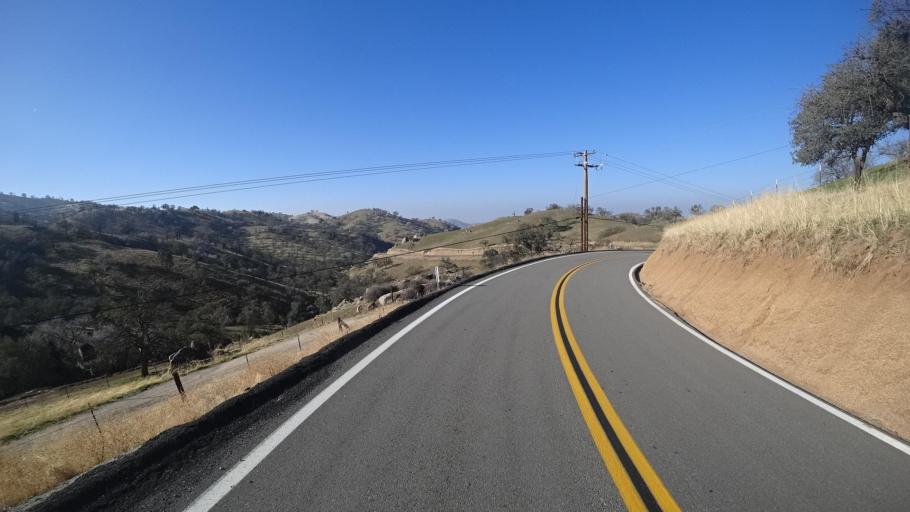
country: US
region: California
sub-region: Kern County
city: Alta Sierra
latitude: 35.7173
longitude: -118.8088
